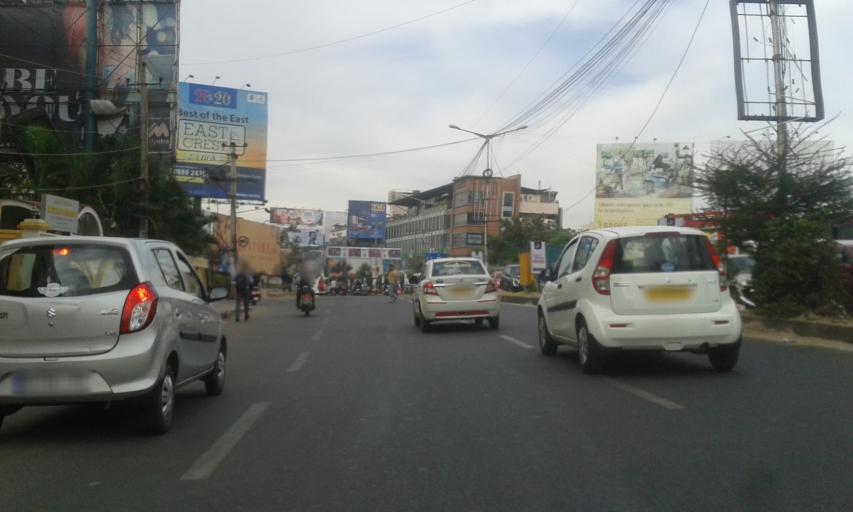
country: IN
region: Karnataka
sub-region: Bangalore Urban
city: Bangalore
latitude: 12.9384
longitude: 77.6292
